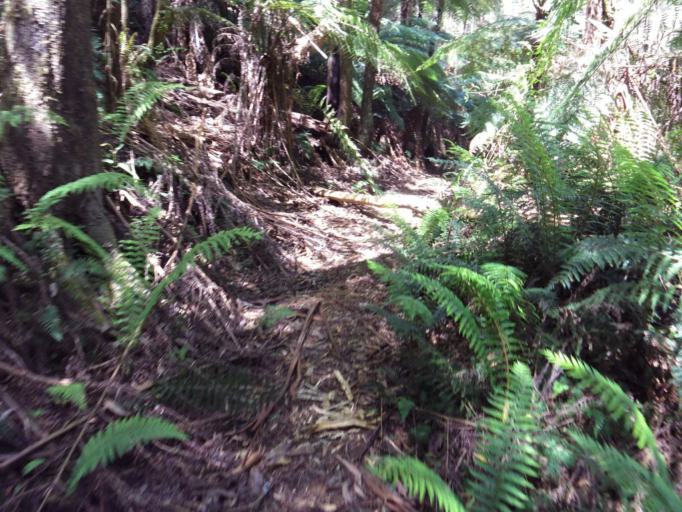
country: AU
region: Victoria
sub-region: Yarra Ranges
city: Millgrove
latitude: -37.8561
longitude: 145.7615
